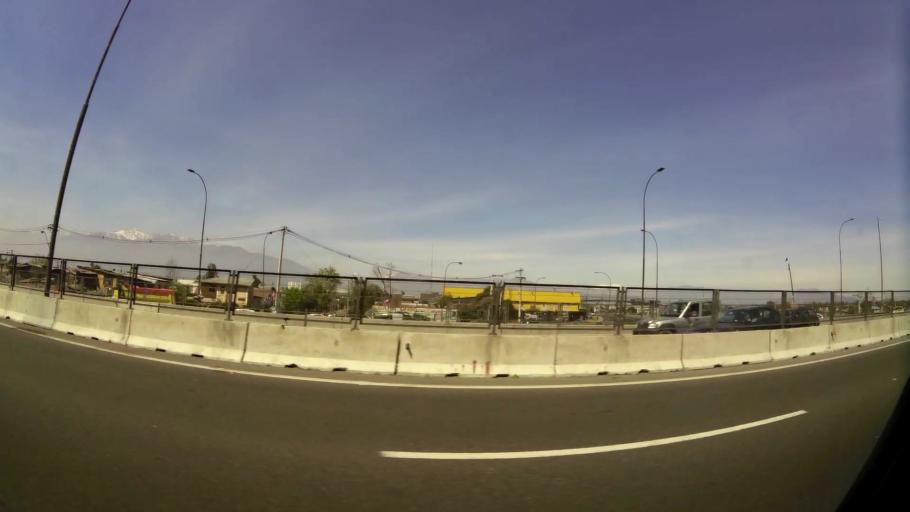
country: CL
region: Santiago Metropolitan
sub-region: Provincia de Maipo
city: San Bernardo
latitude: -33.5313
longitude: -70.6813
